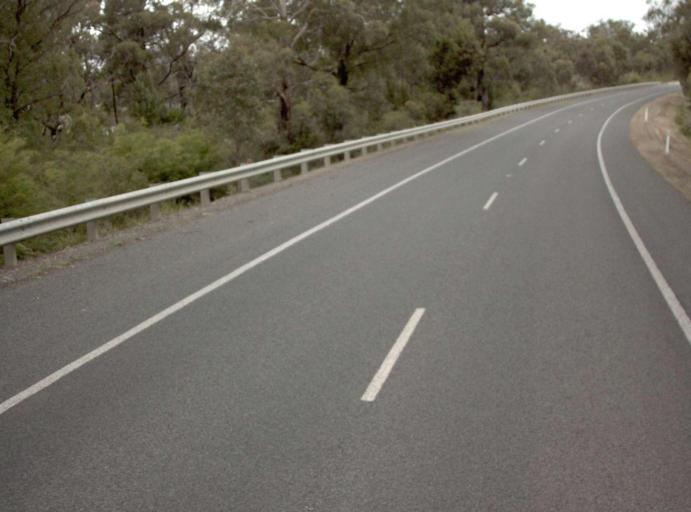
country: AU
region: Victoria
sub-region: Wellington
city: Sale
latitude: -38.3315
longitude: 147.0176
